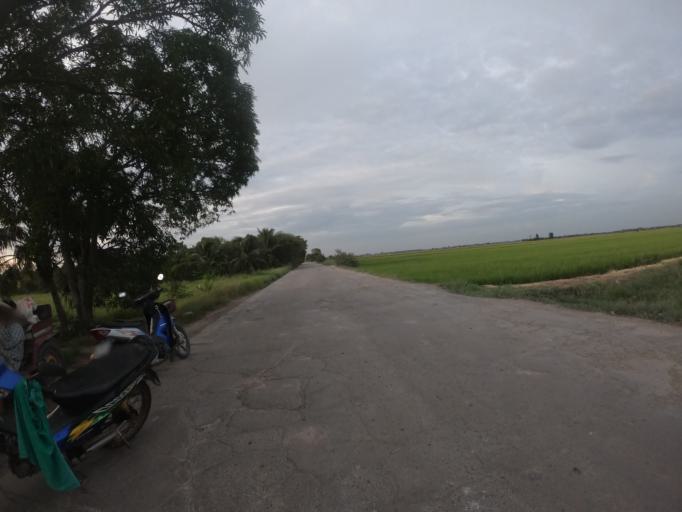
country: TH
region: Pathum Thani
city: Ban Lam Luk Ka
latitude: 13.9986
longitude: 100.7999
